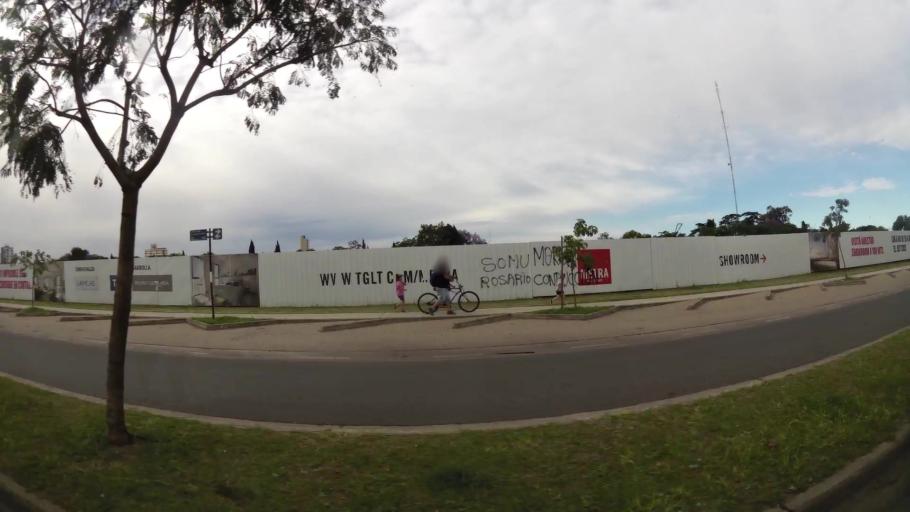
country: AR
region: Santa Fe
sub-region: Departamento de Rosario
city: Rosario
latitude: -32.9215
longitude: -60.6703
